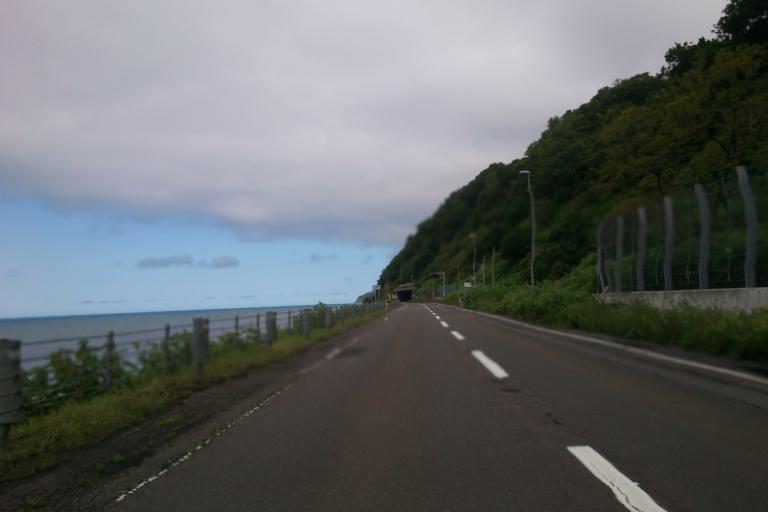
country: JP
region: Hokkaido
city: Ishikari
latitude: 43.4349
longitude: 141.4185
